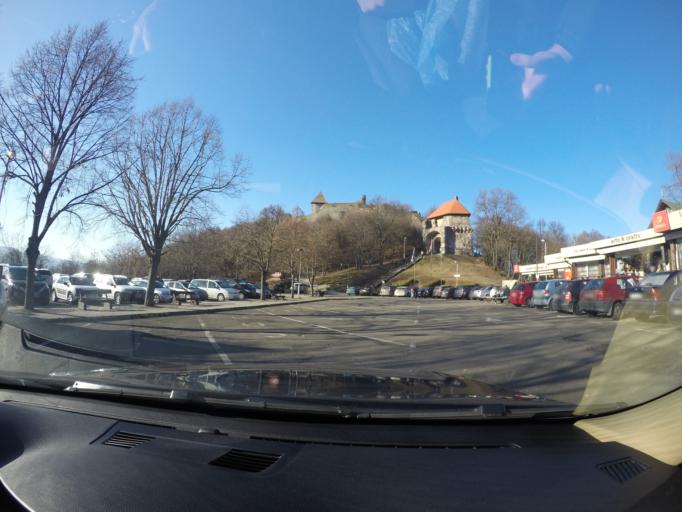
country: HU
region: Pest
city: Visegrad
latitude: 47.7935
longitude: 18.9826
